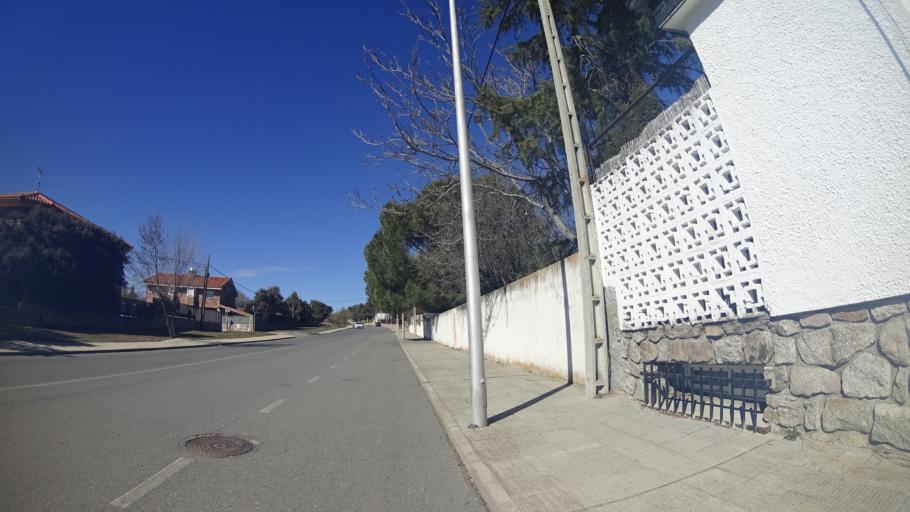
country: ES
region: Madrid
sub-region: Provincia de Madrid
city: Colmenarejo
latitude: 40.5503
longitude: -4.0032
